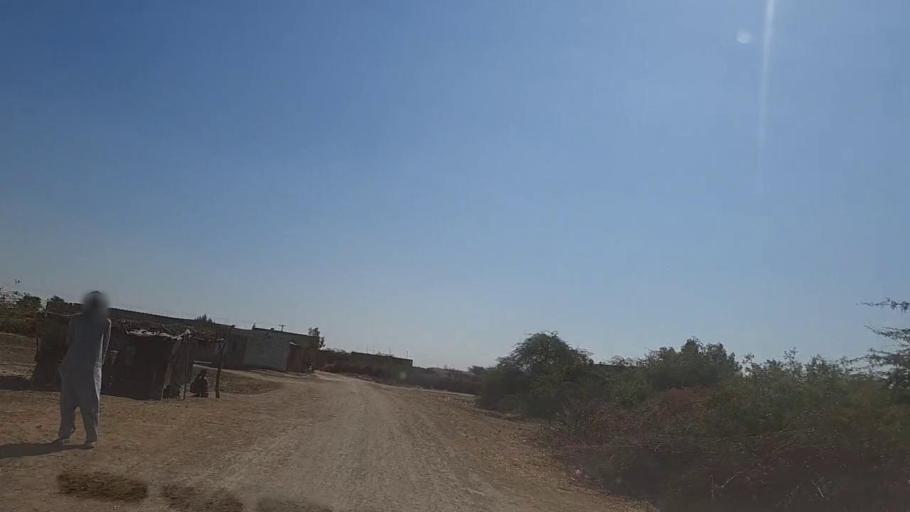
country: PK
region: Sindh
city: Digri
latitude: 25.1005
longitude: 69.1280
